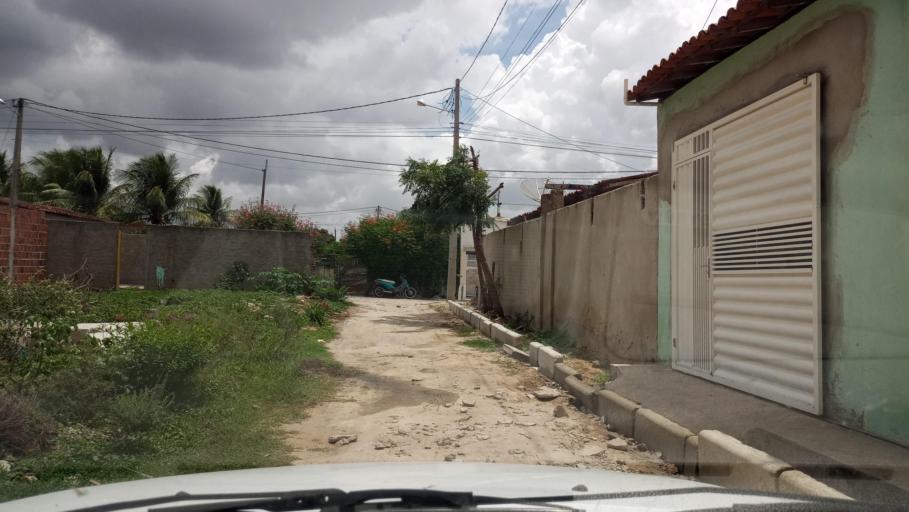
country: BR
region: Rio Grande do Norte
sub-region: Tangara
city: Tangara
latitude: -6.0990
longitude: -35.7126
